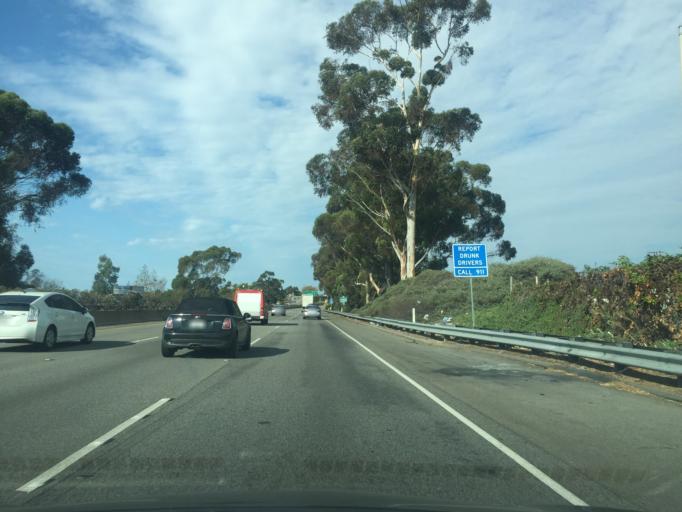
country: US
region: California
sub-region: Santa Barbara County
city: Goleta
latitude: 34.4422
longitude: -119.7813
